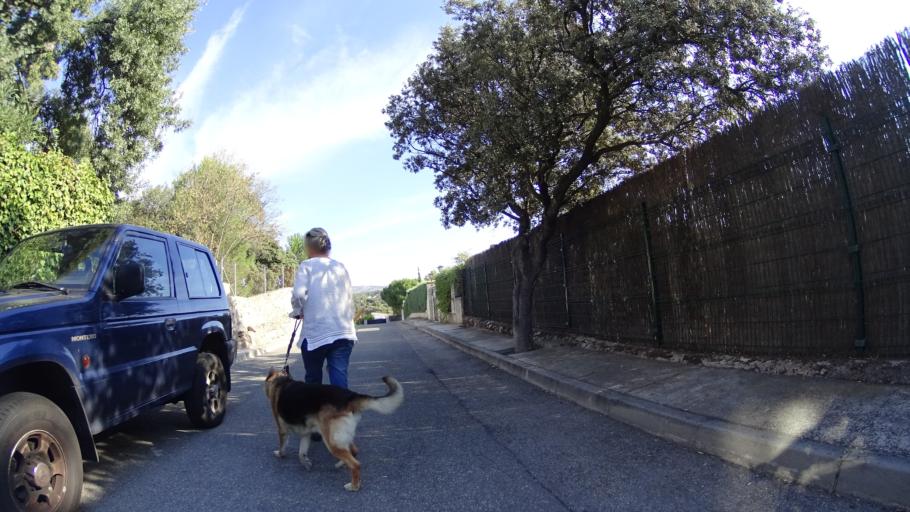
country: ES
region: Madrid
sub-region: Provincia de Madrid
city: Galapagar
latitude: 40.5853
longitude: -3.9727
